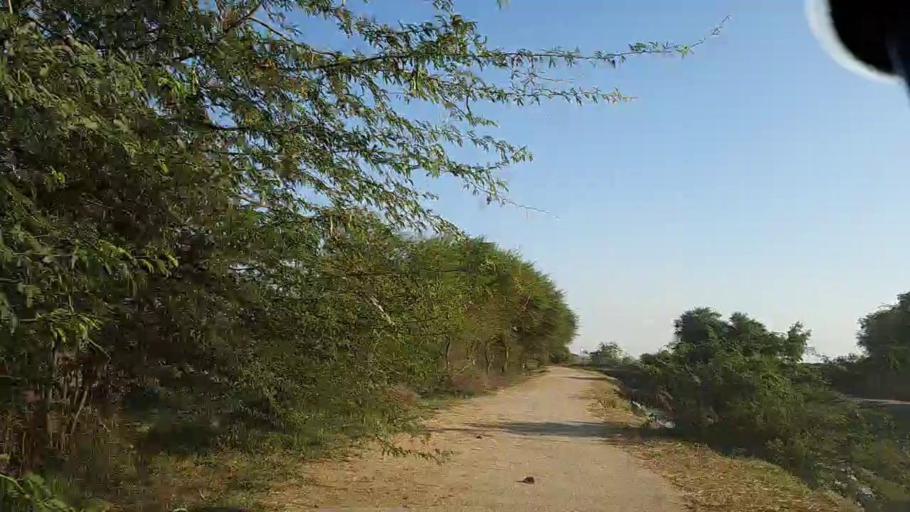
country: PK
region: Sindh
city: Chuhar Jamali
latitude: 24.5624
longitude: 68.0687
